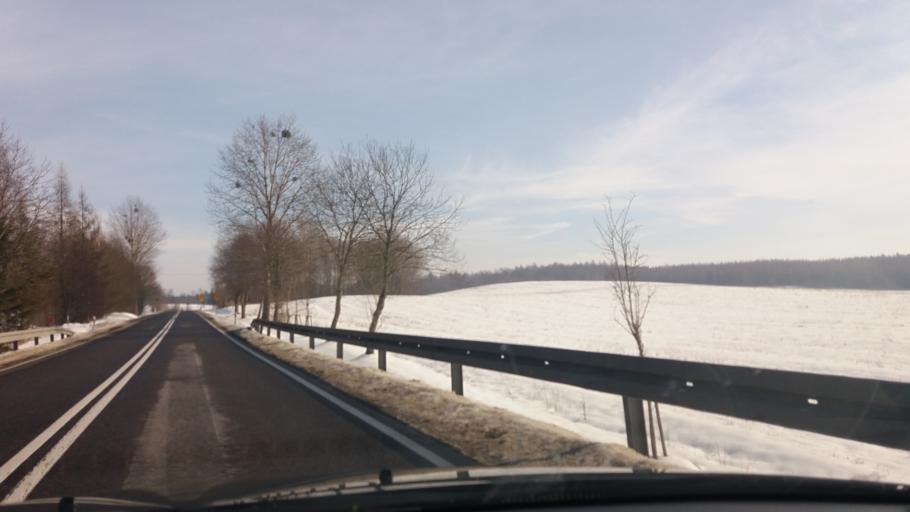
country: PL
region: Warmian-Masurian Voivodeship
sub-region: Powiat olsztynski
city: Czerwonka
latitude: 53.9450
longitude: 20.8968
